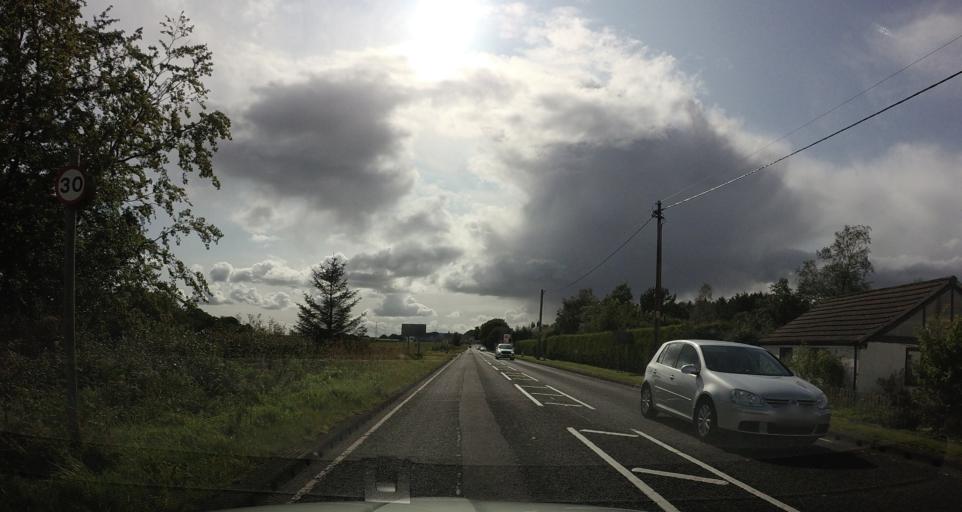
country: GB
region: Scotland
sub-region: Fife
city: Saline
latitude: 56.1870
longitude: -3.5468
